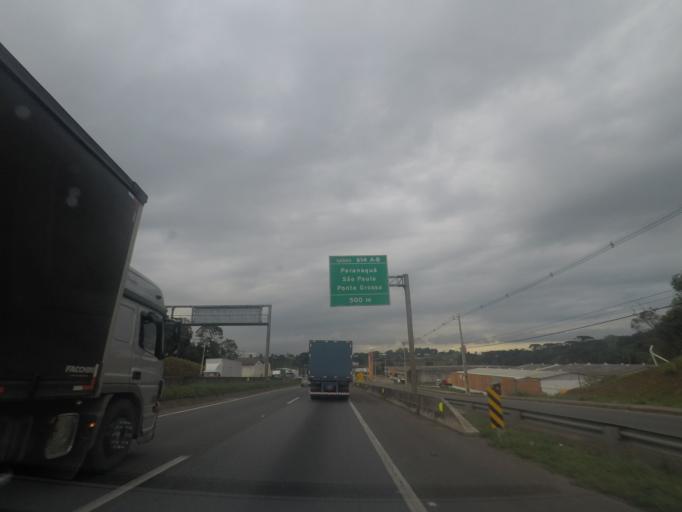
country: BR
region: Parana
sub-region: Sao Jose Dos Pinhais
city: Sao Jose dos Pinhais
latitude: -25.5790
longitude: -49.1783
